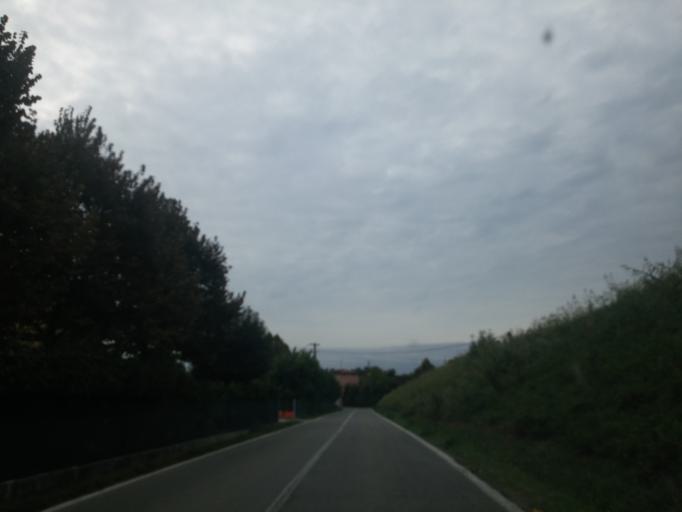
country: IT
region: Emilia-Romagna
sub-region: Provincia di Bologna
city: Longara
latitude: 44.5989
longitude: 11.3172
